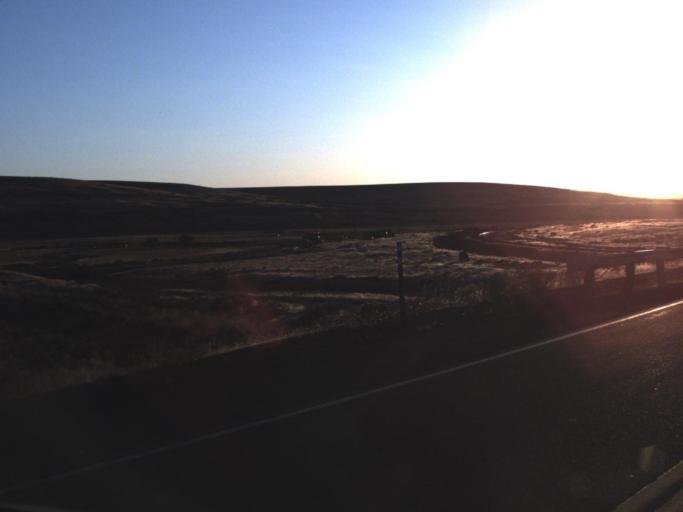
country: US
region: Washington
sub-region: Adams County
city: Ritzville
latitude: 46.9701
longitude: -118.5722
